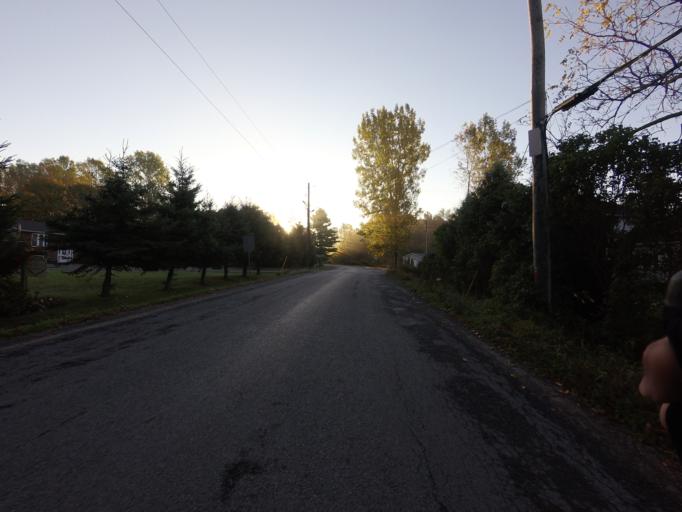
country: CA
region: Ontario
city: Quinte West
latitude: 44.0328
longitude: -77.5785
